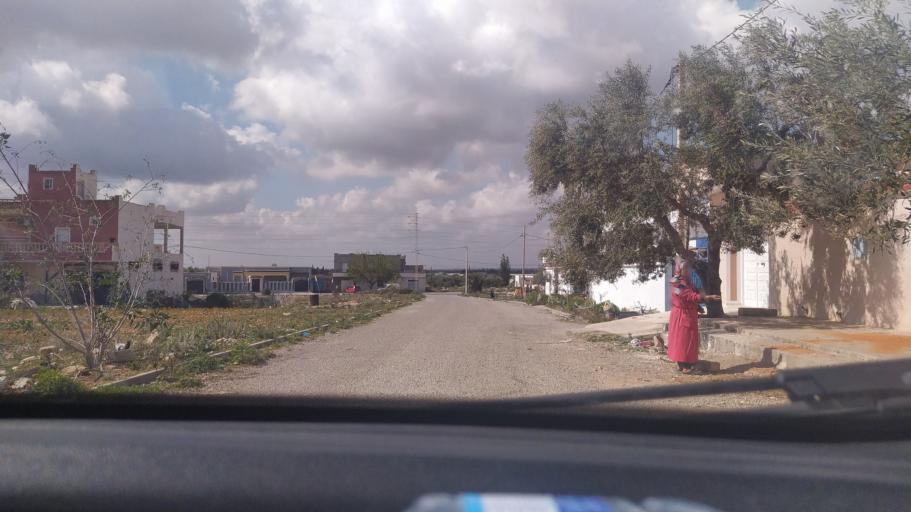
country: TN
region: Al Munastir
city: Sidi Bin Nur
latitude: 35.5244
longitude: 10.9397
